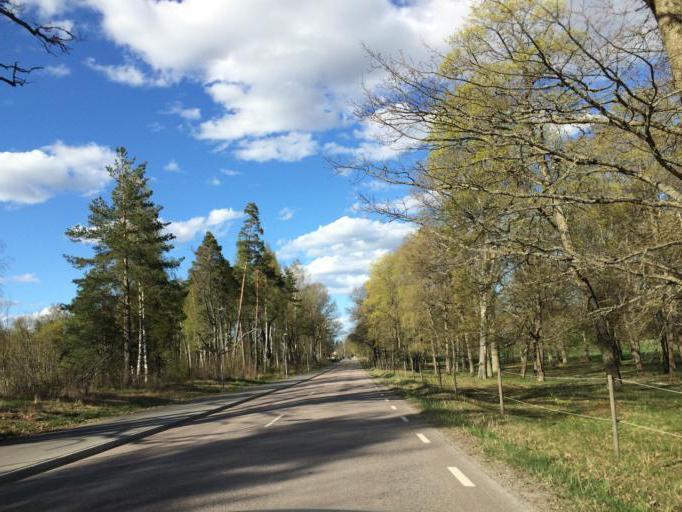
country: SE
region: Soedermanland
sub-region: Eskilstuna Kommun
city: Hallbybrunn
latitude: 59.3656
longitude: 16.4382
